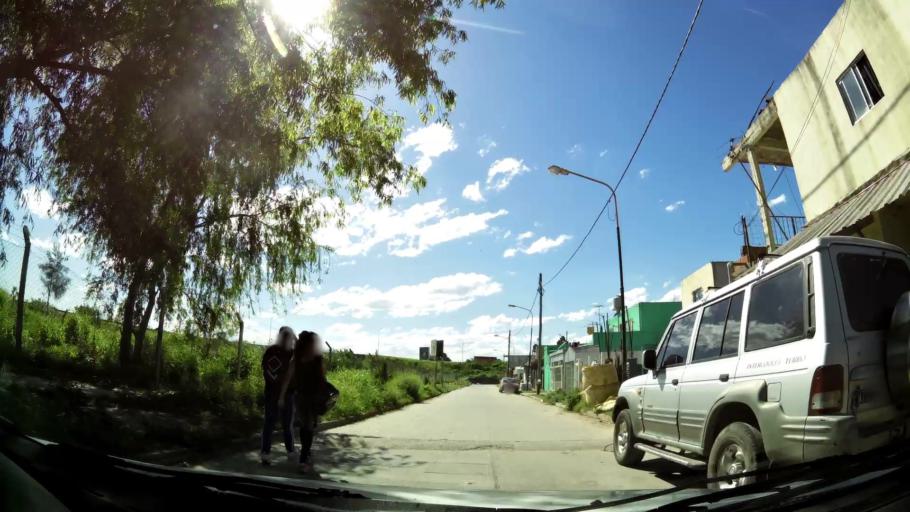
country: AR
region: Buenos Aires
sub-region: Partido de Tigre
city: Tigre
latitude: -34.5109
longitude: -58.5884
